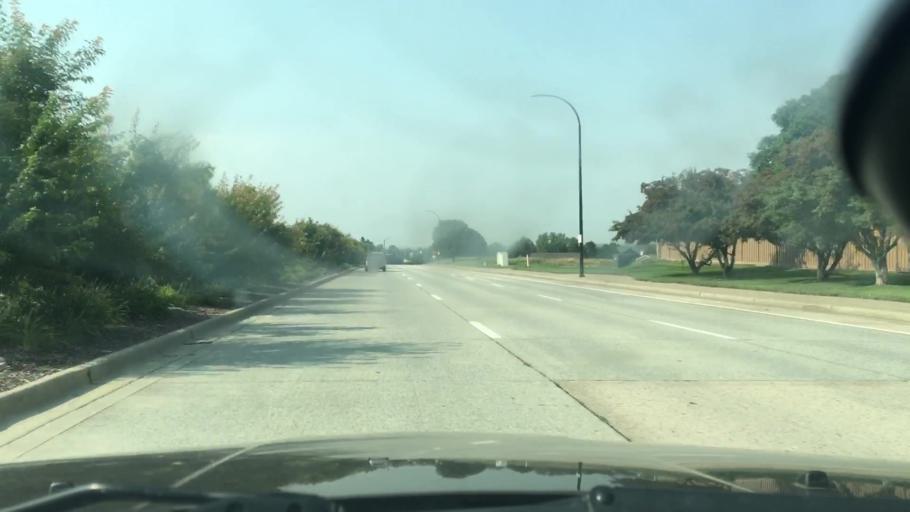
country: US
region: Colorado
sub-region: Douglas County
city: Acres Green
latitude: 39.5518
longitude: -104.9110
